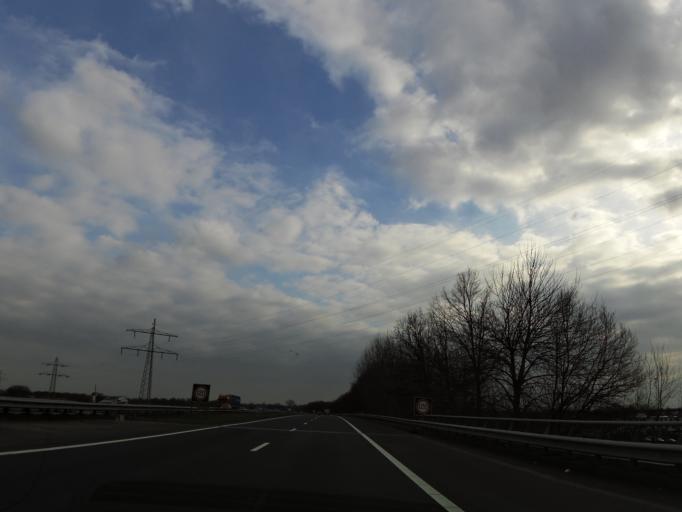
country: NL
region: Limburg
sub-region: Gemeente Nederweert
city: Nederweert
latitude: 51.2699
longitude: 5.7401
